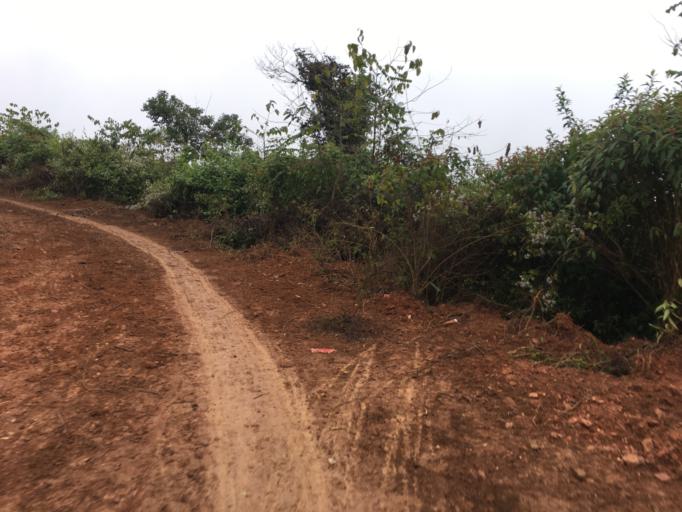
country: LA
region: Houaphan
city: Xamtay
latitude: 19.8955
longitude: 104.4635
